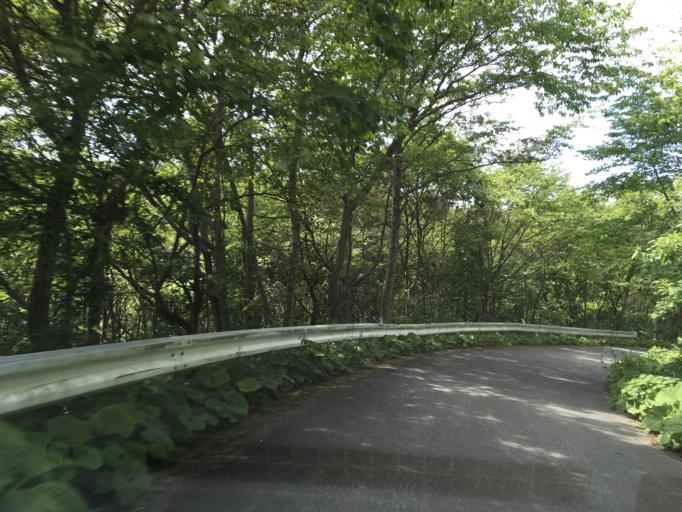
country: JP
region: Iwate
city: Mizusawa
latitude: 39.1371
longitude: 141.3040
